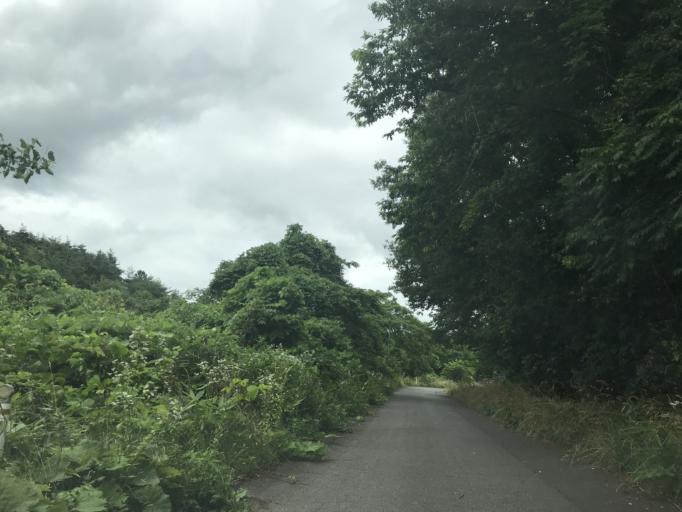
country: JP
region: Iwate
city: Ichinoseki
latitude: 38.9083
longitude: 141.0067
